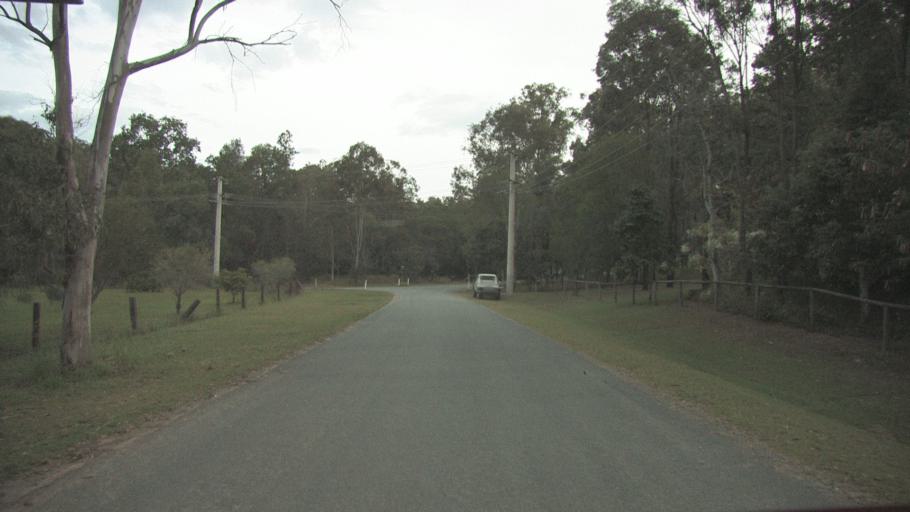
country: AU
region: Queensland
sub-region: Logan
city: Chambers Flat
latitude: -27.8199
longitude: 153.0917
